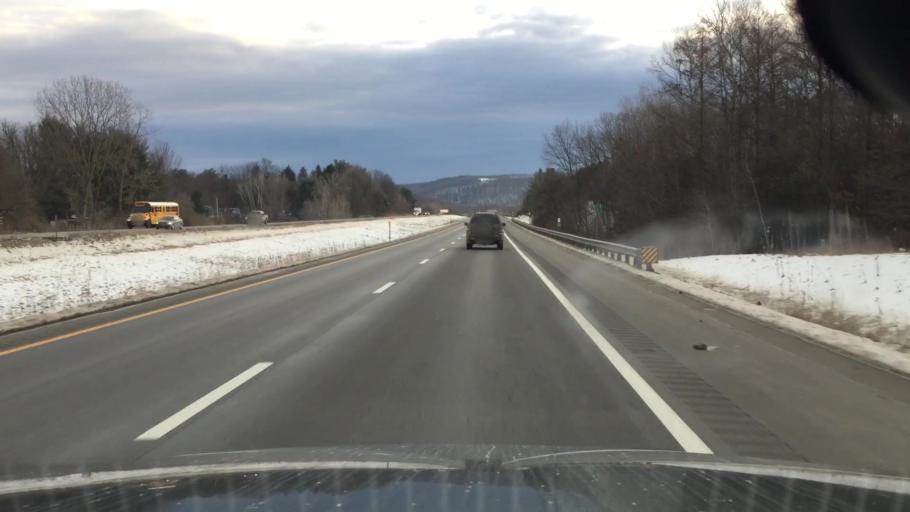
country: US
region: New York
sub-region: Tioga County
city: Waverly
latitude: 42.0036
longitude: -76.4975
